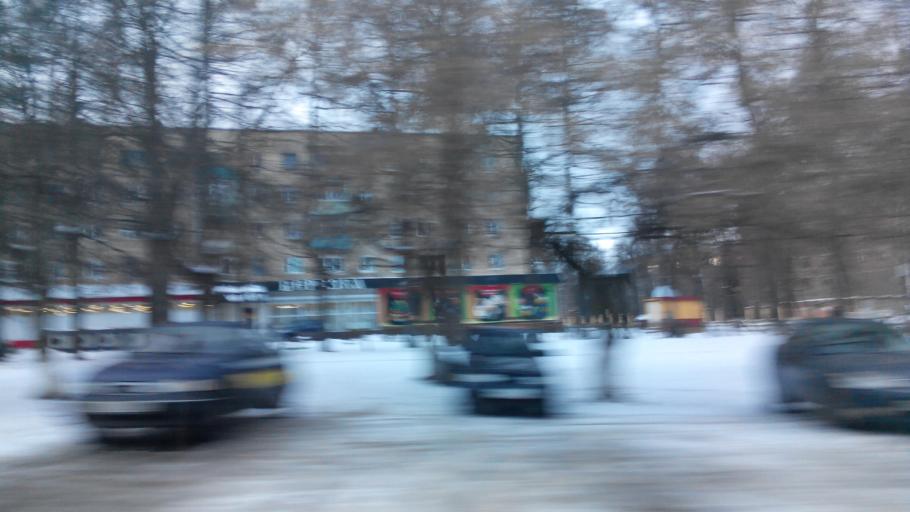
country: RU
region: Tula
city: Uzlovaya
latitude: 53.9756
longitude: 38.1880
